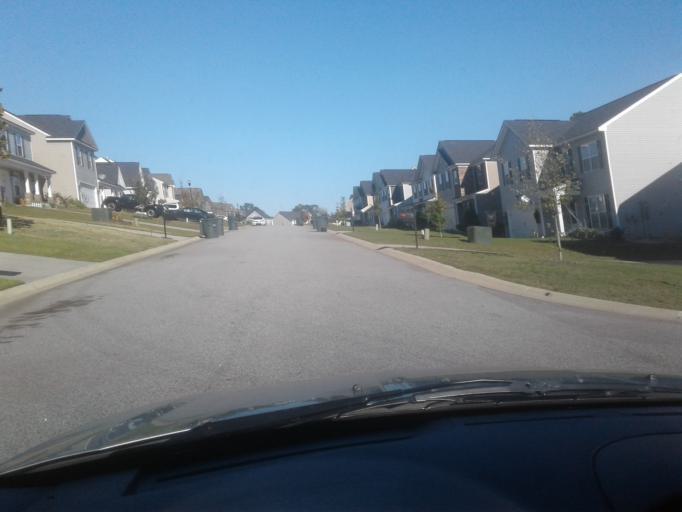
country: US
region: South Carolina
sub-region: Richland County
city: Woodfield
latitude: 34.0808
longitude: -80.8877
